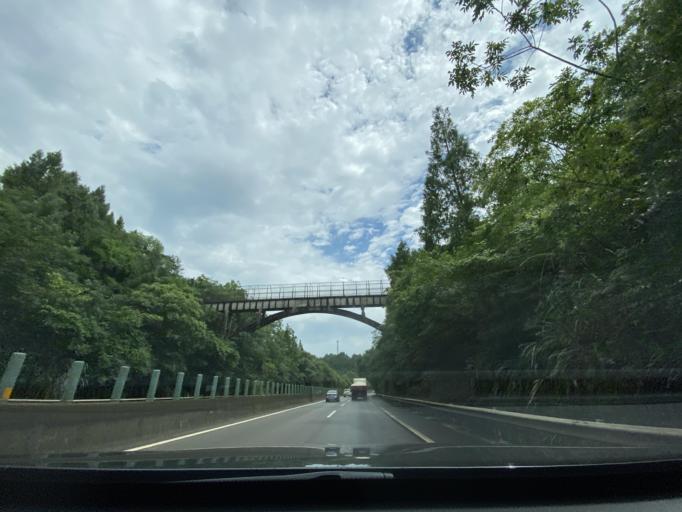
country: CN
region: Sichuan
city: Jiancheng
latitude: 30.3152
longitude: 104.5764
